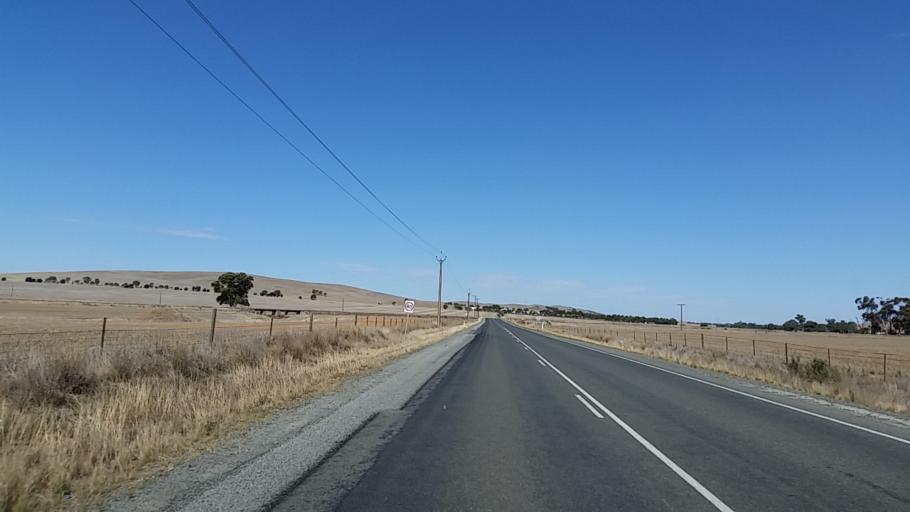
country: AU
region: South Australia
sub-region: Clare and Gilbert Valleys
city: Clare
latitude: -33.6852
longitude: 138.9059
